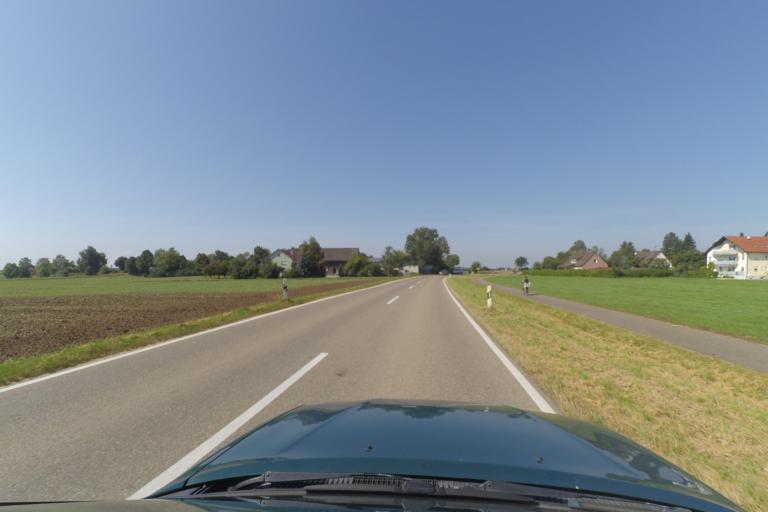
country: DE
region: Bavaria
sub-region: Swabia
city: Hochstadt an der Donau
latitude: 48.6150
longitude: 10.5407
